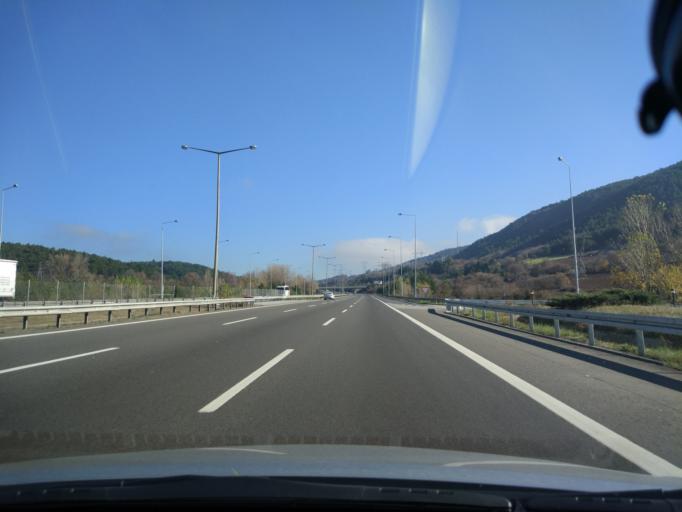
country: TR
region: Bolu
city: Yenicaga
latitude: 40.7431
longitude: 31.8604
